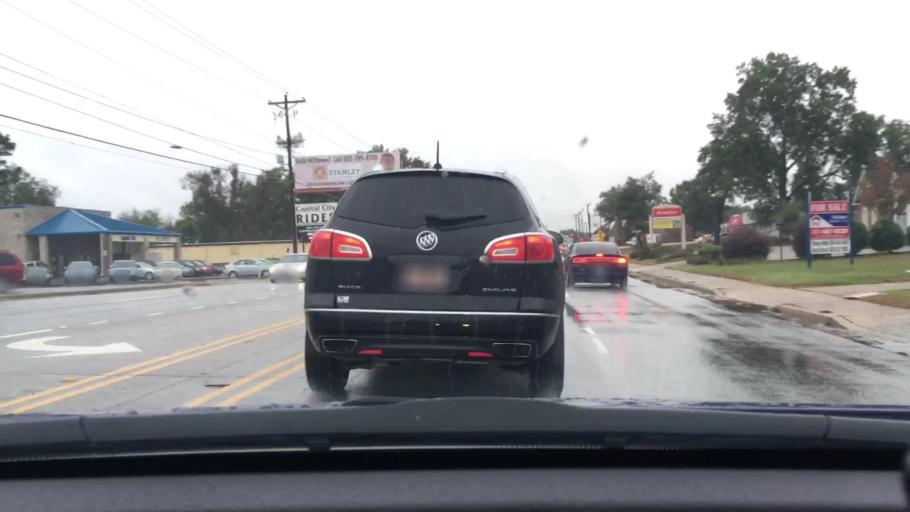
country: US
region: South Carolina
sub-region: Lexington County
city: West Columbia
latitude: 34.0276
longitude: -81.0839
